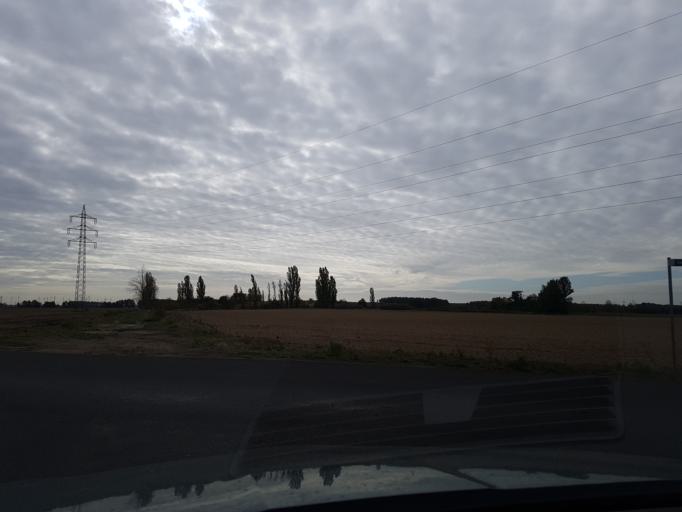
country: DE
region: Brandenburg
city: Falkenberg
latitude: 51.5641
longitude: 13.2491
